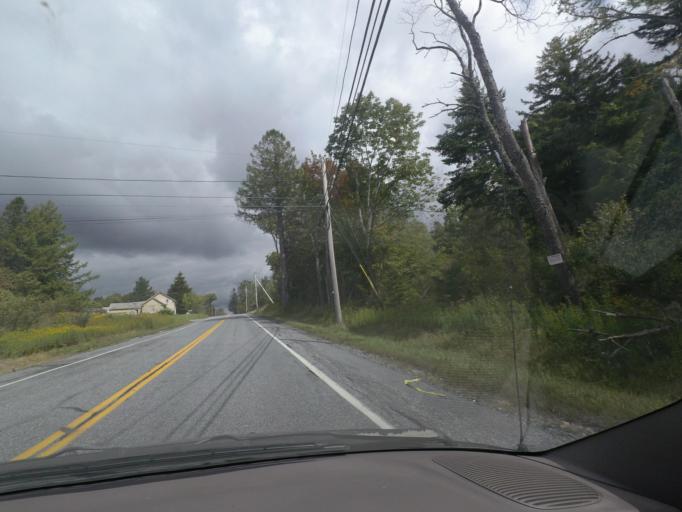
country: US
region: Vermont
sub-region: Bennington County
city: Bennington
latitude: 42.8845
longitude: -73.0775
